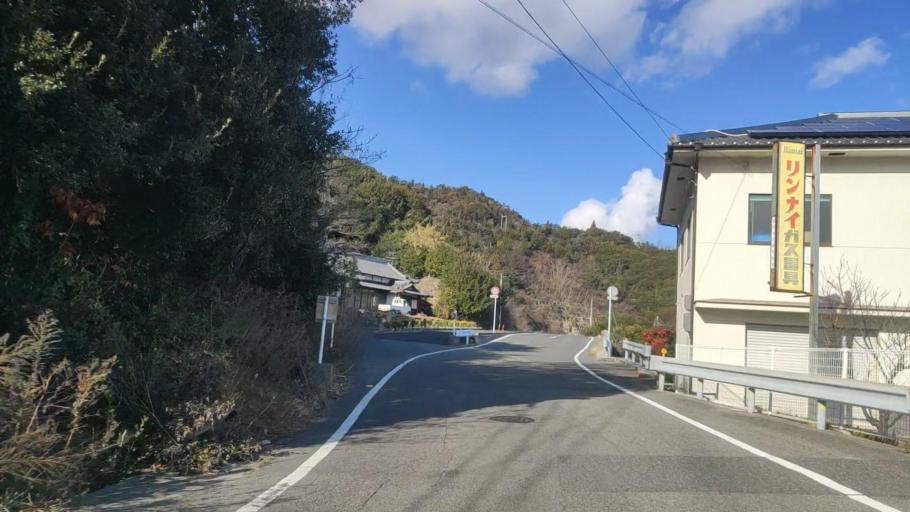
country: JP
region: Hiroshima
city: Innoshima
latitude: 34.2241
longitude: 133.1082
